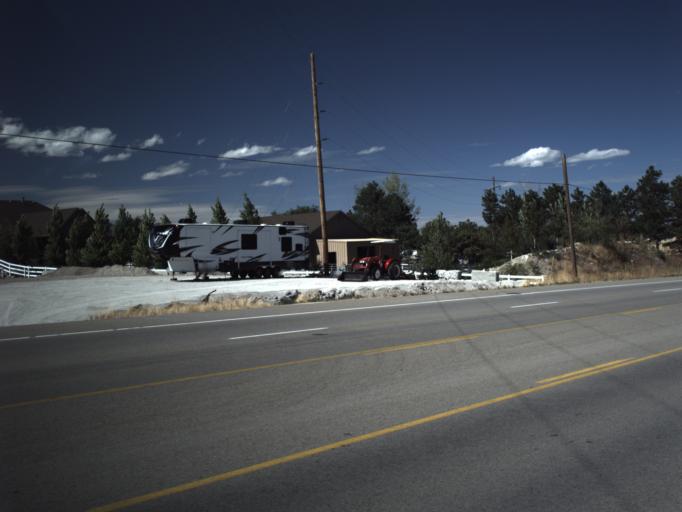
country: US
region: Utah
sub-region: Salt Lake County
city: Bluffdale
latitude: 40.4730
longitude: -111.9468
